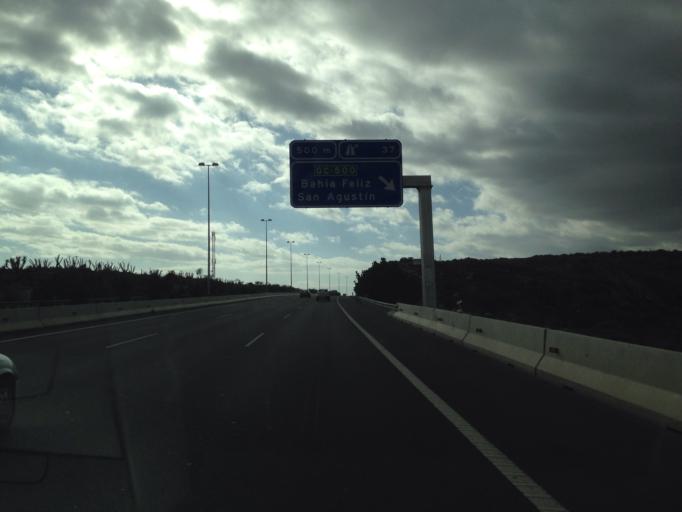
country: ES
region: Canary Islands
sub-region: Provincia de Las Palmas
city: Playa del Ingles
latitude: 27.7910
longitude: -15.4984
